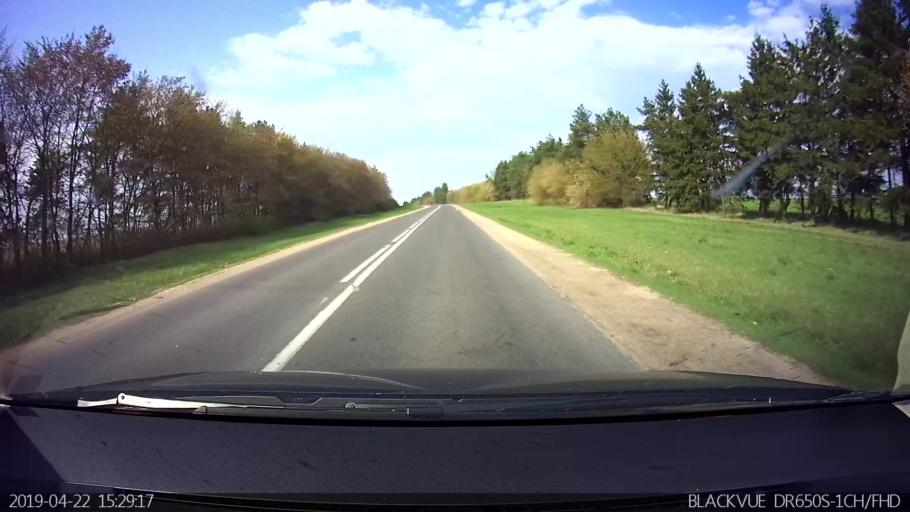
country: BY
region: Brest
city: Vysokaye
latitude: 52.3839
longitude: 23.3722
